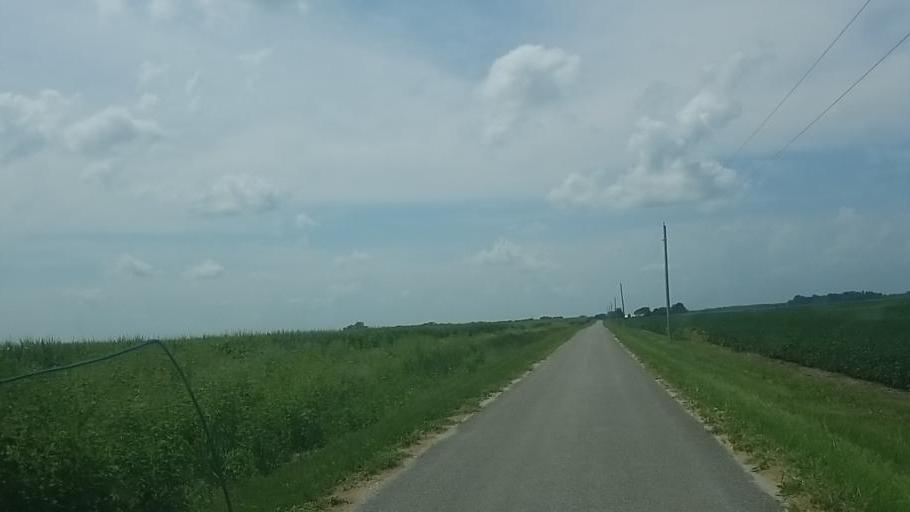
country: US
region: Ohio
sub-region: Wyandot County
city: Upper Sandusky
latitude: 40.6731
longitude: -83.2790
